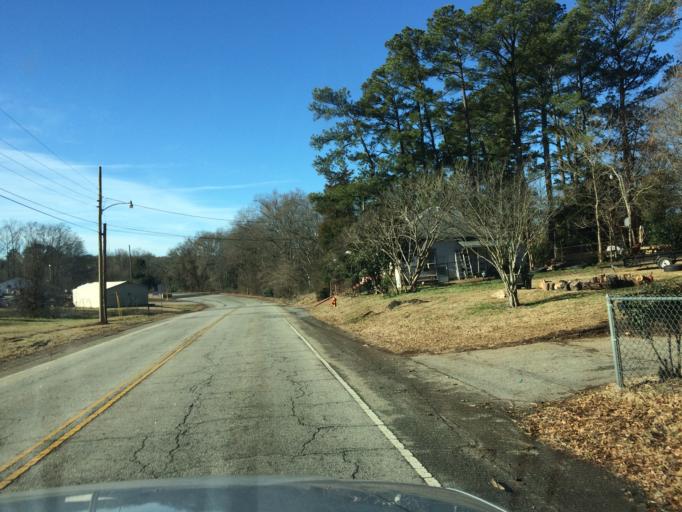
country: US
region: South Carolina
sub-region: Spartanburg County
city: Arcadia
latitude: 34.9601
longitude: -81.9924
